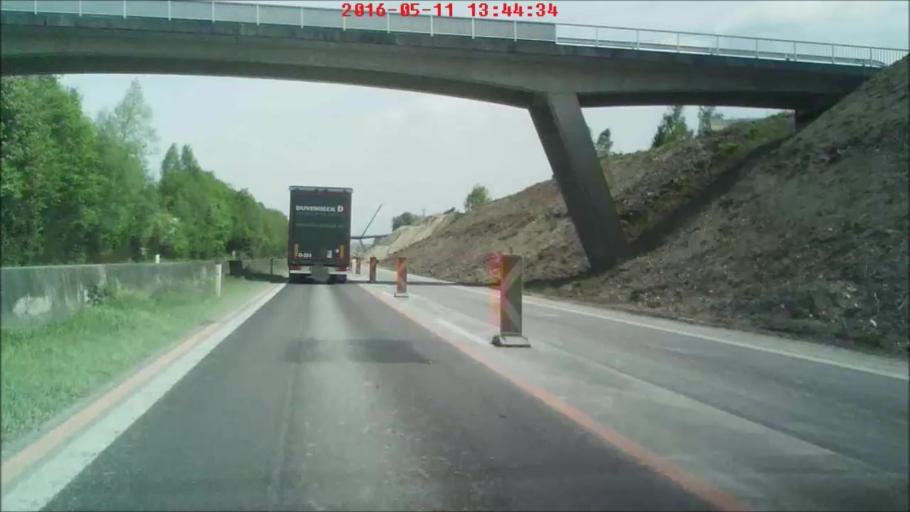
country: AT
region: Upper Austria
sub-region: Politischer Bezirk Ried im Innkreis
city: Ried im Innkreis
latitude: 48.2242
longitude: 13.6088
